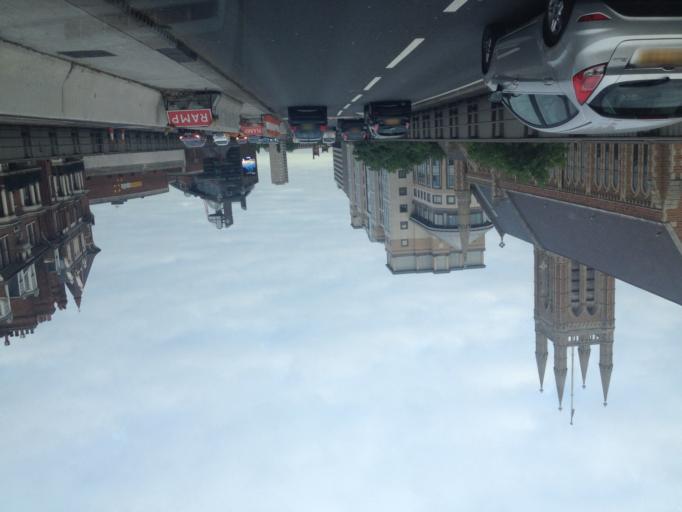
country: GB
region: England
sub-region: Greater London
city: Hammersmith
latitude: 51.4913
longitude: -0.2264
